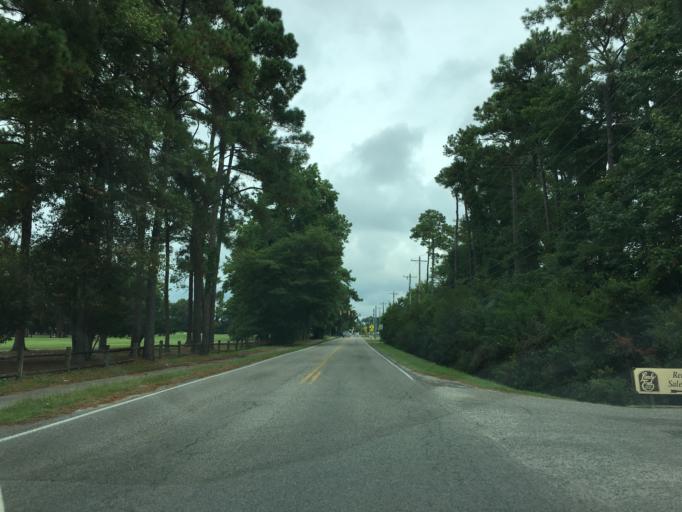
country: US
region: South Carolina
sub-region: Horry County
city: North Myrtle Beach
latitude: 33.7800
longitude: -78.7714
